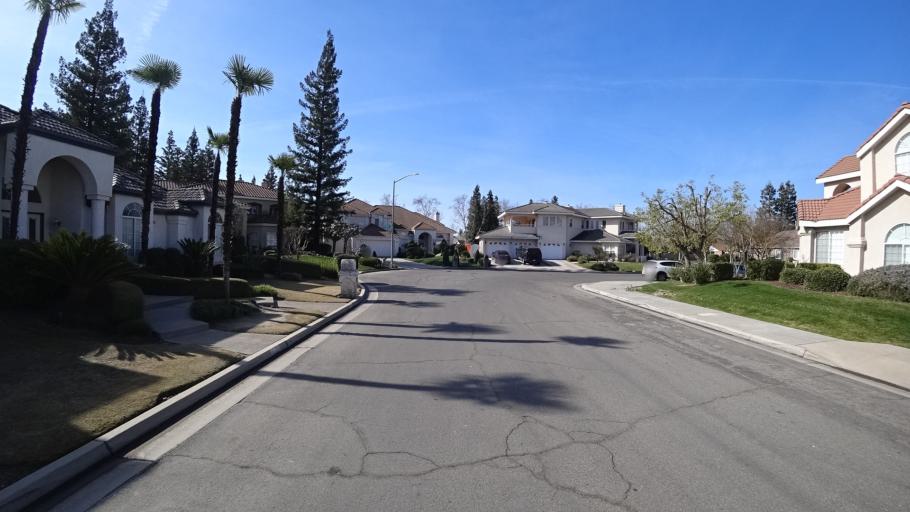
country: US
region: California
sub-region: Fresno County
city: Clovis
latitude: 36.8911
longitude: -119.7686
